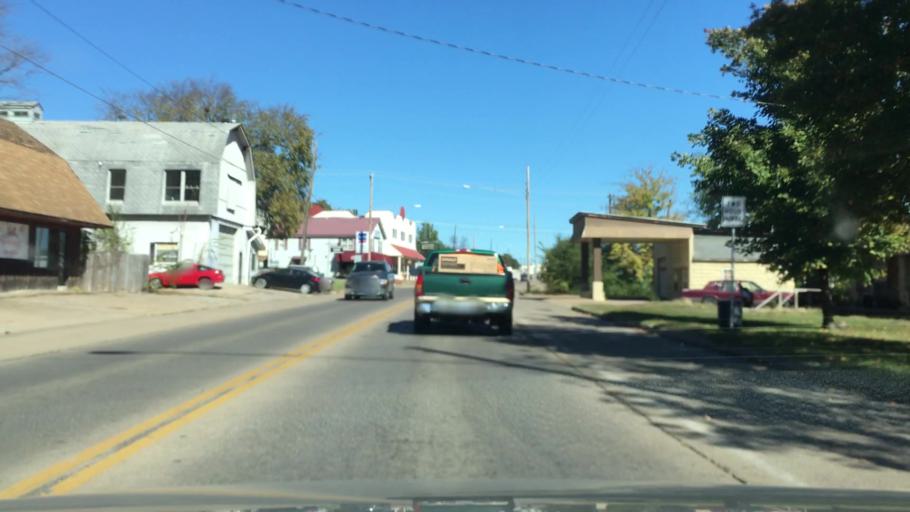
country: US
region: Oklahoma
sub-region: Cherokee County
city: Tahlequah
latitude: 35.9064
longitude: -94.9741
